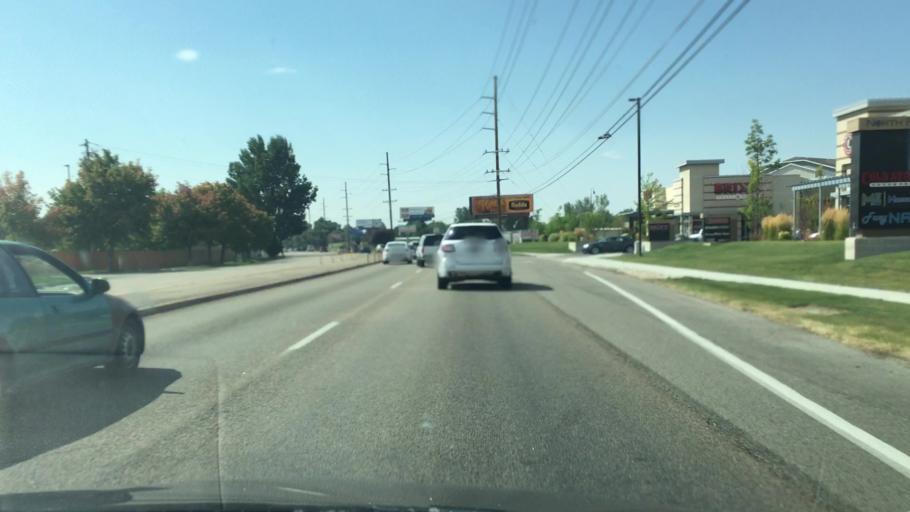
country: US
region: Idaho
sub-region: Ada County
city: Garden City
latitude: 43.6709
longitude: -116.2829
